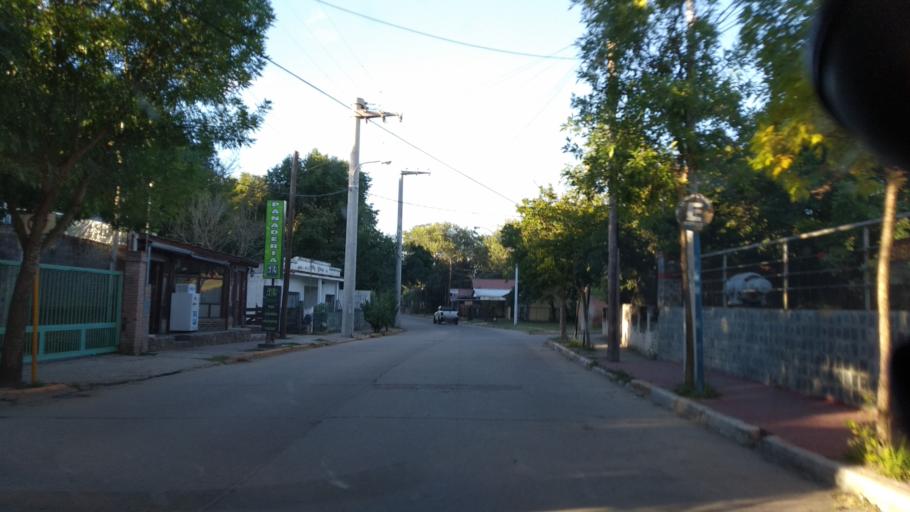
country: AR
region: Cordoba
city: Mina Clavero
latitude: -31.7156
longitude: -65.0060
